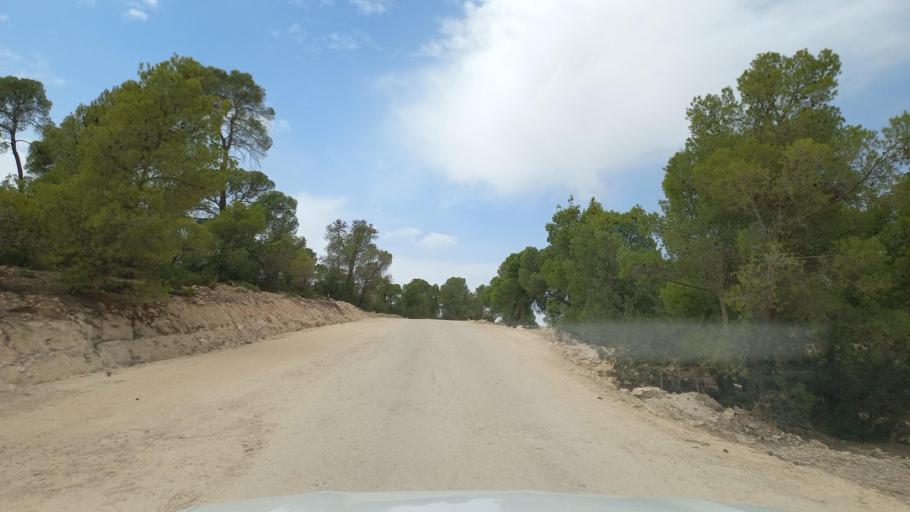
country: TN
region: Al Qasrayn
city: Kasserine
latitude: 35.3812
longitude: 8.8824
